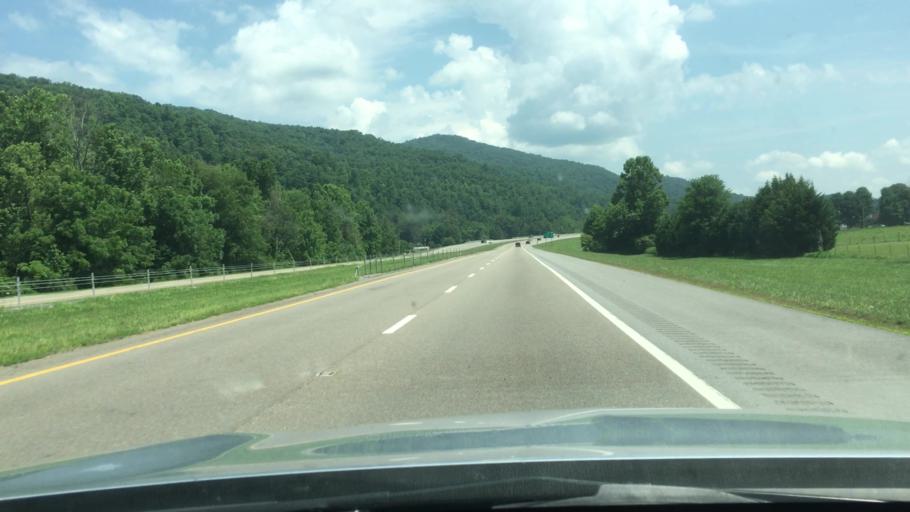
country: US
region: Tennessee
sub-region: Unicoi County
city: Unicoi
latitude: 36.1817
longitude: -82.3809
